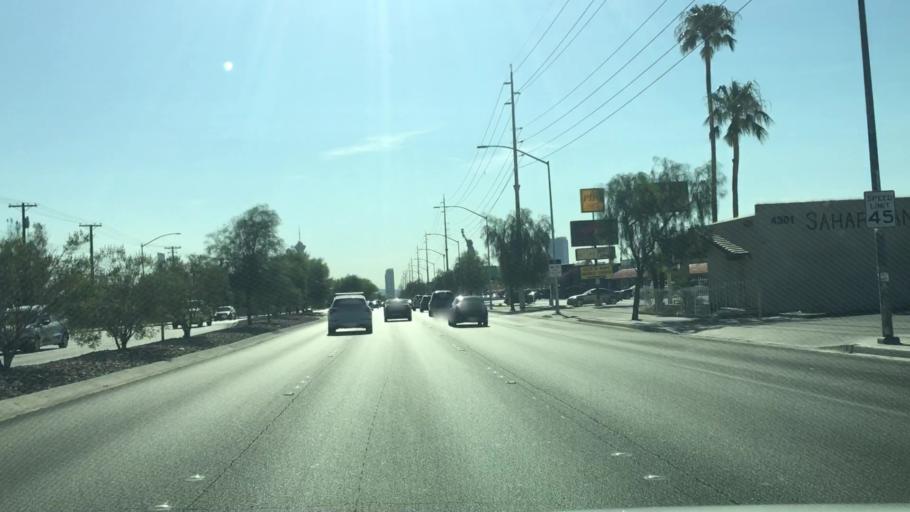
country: US
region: Nevada
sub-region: Clark County
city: Spring Valley
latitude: 36.1444
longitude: -115.1995
